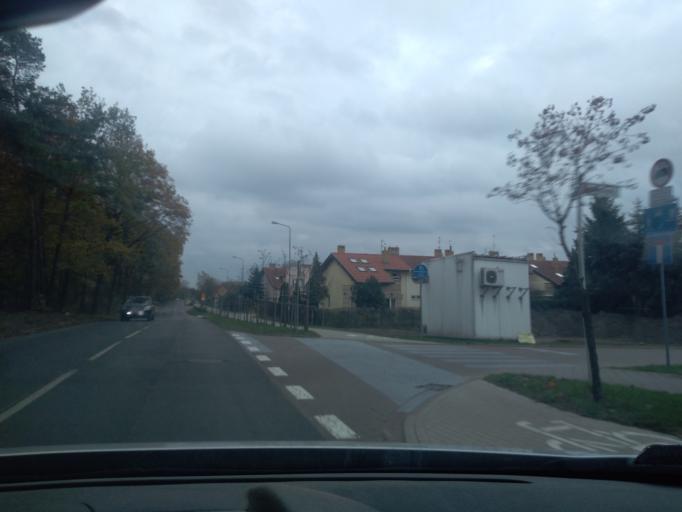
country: PL
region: Greater Poland Voivodeship
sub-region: Powiat poznanski
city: Suchy Las
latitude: 52.4742
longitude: 16.8961
